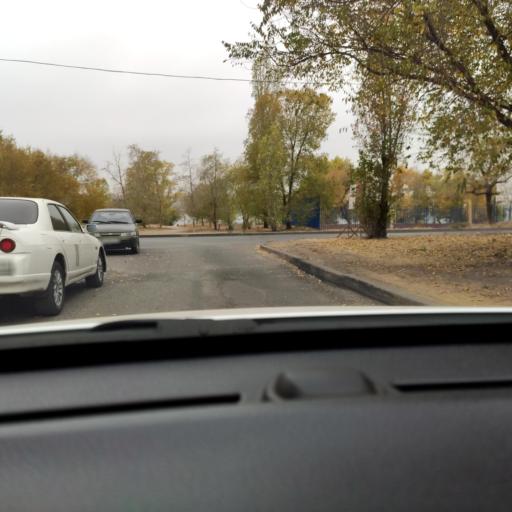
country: RU
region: Voronezj
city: Voronezh
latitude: 51.6964
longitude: 39.2572
